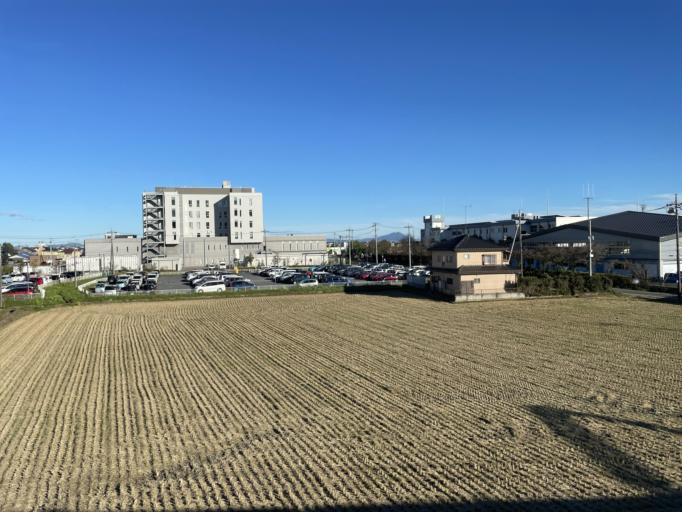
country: JP
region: Tochigi
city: Tochigi
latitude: 36.3661
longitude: 139.7247
